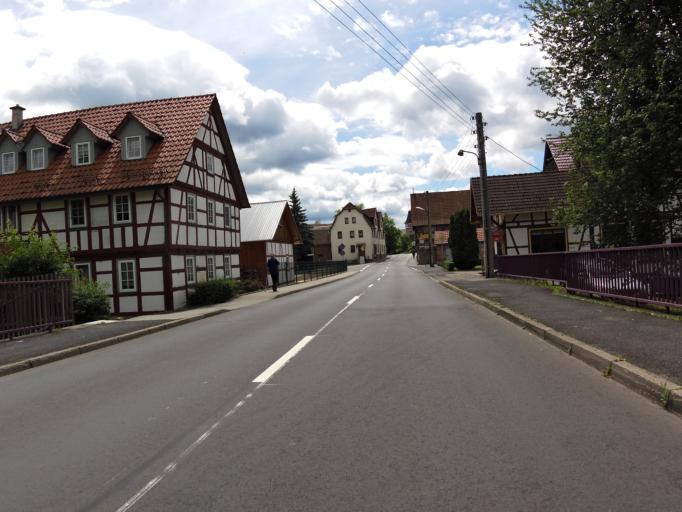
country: DE
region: Thuringia
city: Wernshausen
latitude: 50.7249
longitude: 10.3511
